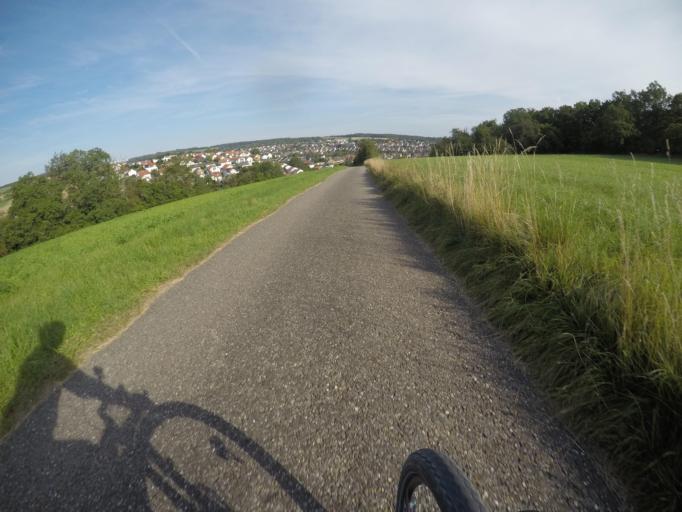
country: DE
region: Baden-Wuerttemberg
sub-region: Regierungsbezirk Stuttgart
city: Weissach
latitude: 48.8409
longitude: 8.9340
